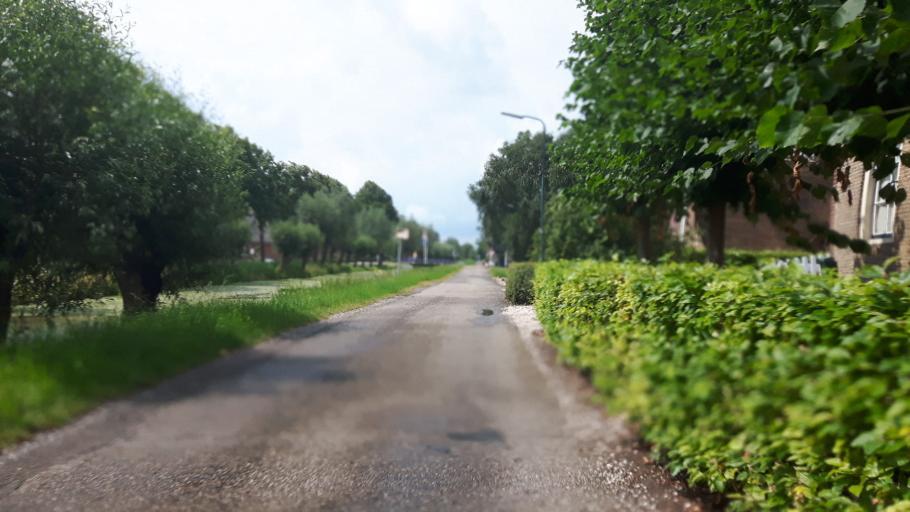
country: NL
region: Utrecht
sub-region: Gemeente Oudewater
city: Oudewater
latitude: 51.9886
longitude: 4.8836
